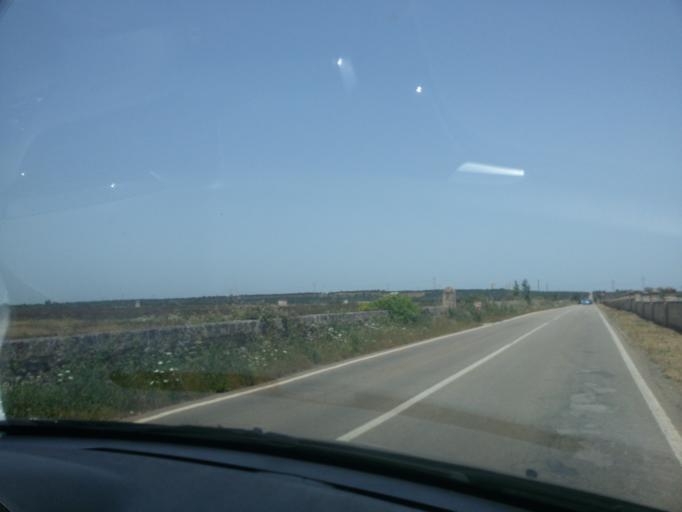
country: IT
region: Apulia
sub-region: Provincia di Lecce
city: Porto Cesareo
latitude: 40.2816
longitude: 17.9069
